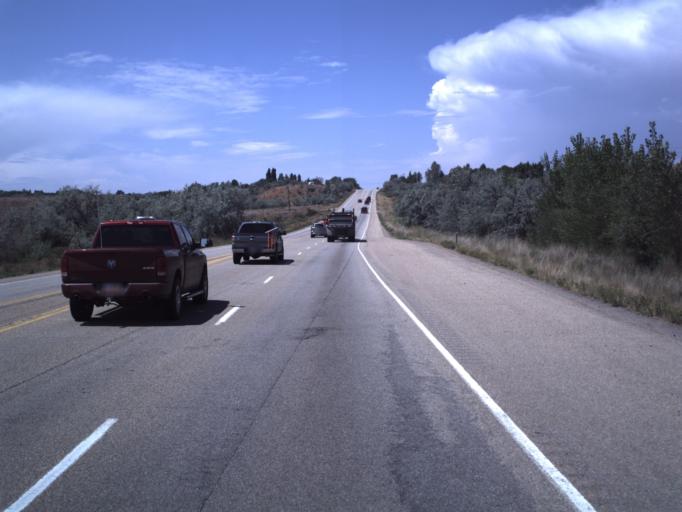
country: US
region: Utah
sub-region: Duchesne County
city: Roosevelt
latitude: 40.3019
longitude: -109.8819
